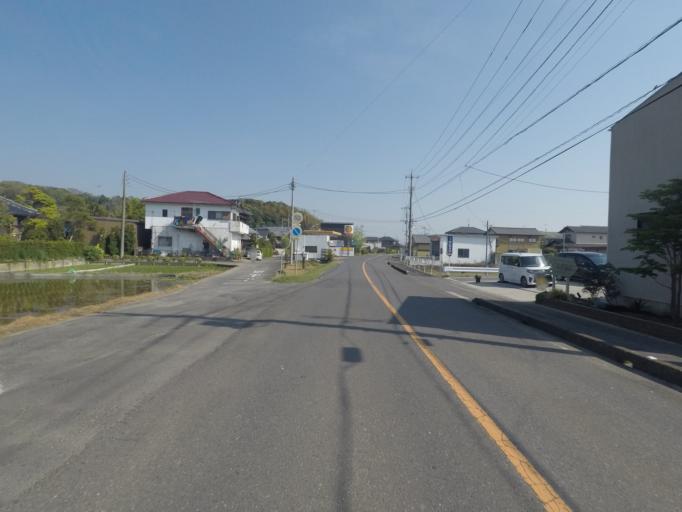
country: JP
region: Ibaraki
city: Itako
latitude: 36.0500
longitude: 140.4483
